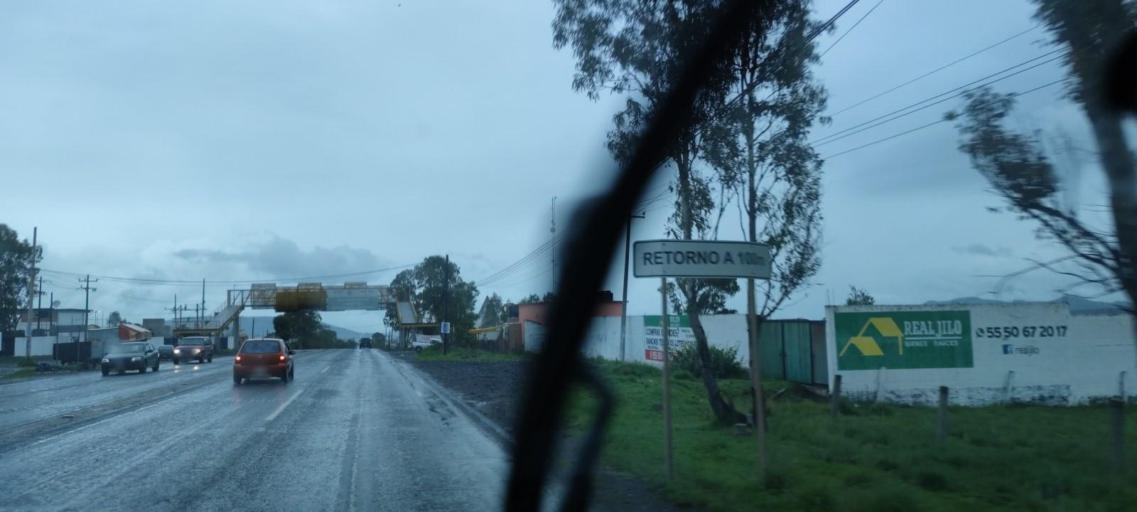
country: MX
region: Mexico
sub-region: Jilotepec
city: Doxhicho
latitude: 19.9420
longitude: -99.5612
